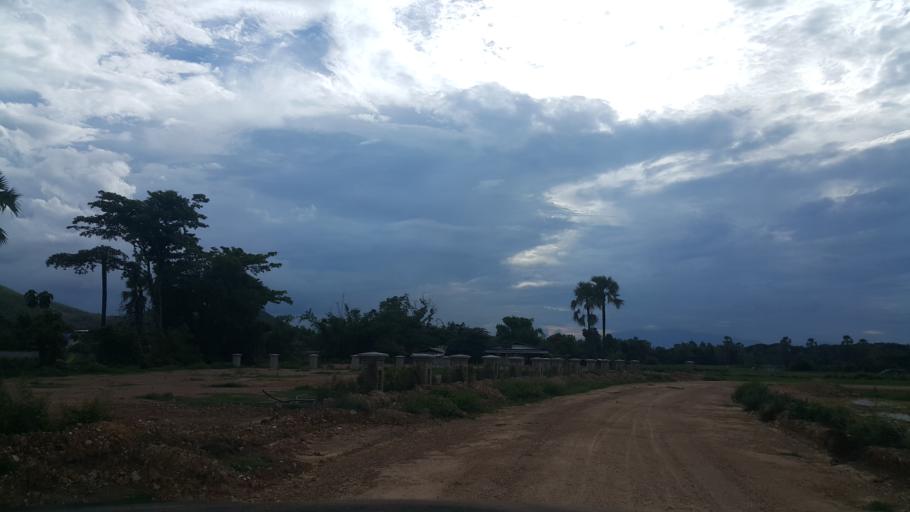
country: TH
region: Chiang Mai
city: Mae On
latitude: 18.7221
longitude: 99.2125
